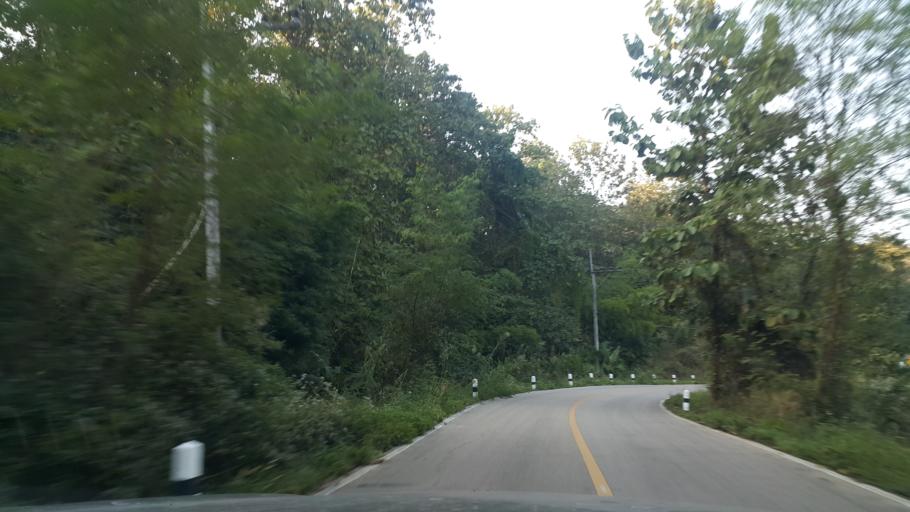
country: TH
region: Lampang
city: Hang Chat
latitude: 18.3472
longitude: 99.2528
